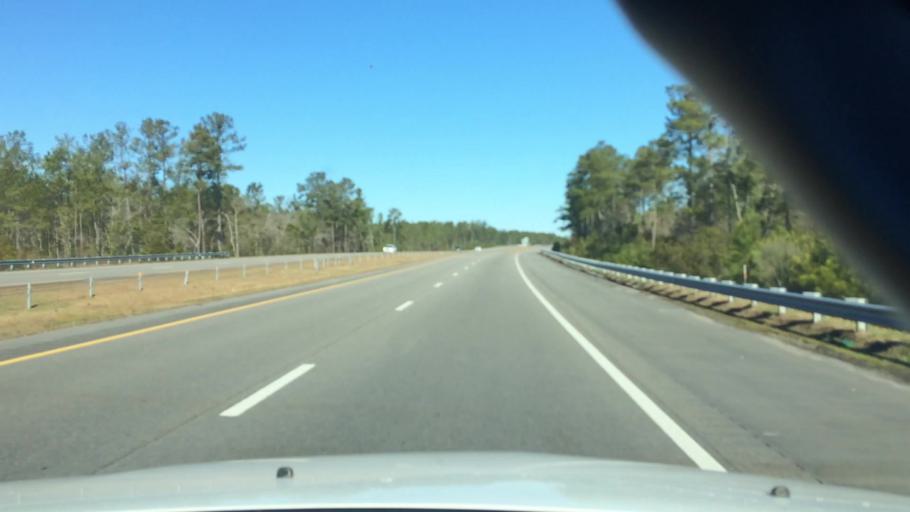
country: US
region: North Carolina
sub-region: Brunswick County
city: Leland
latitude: 34.2132
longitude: -78.0764
